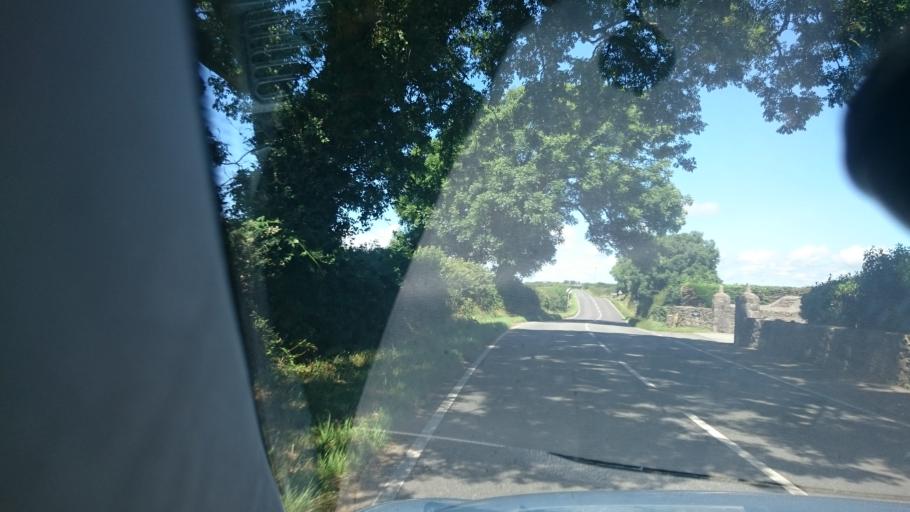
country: GB
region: Wales
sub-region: Pembrokeshire
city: Burton
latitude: 51.7126
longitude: -4.9213
